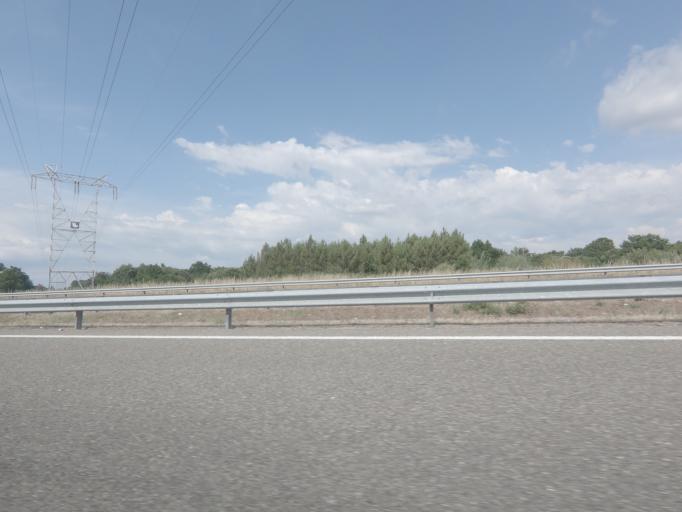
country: ES
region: Galicia
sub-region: Provincia de Ourense
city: Taboadela
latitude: 42.2647
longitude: -7.8692
